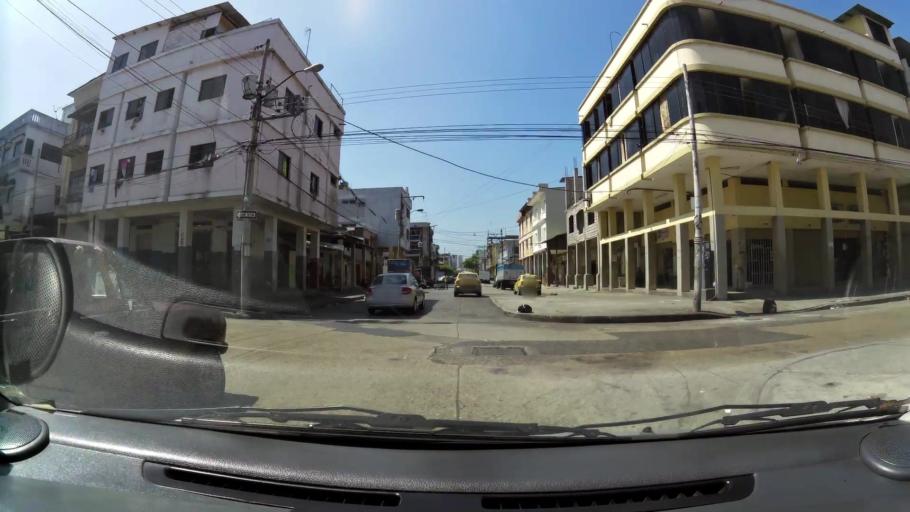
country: EC
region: Guayas
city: Guayaquil
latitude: -2.1954
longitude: -79.8934
